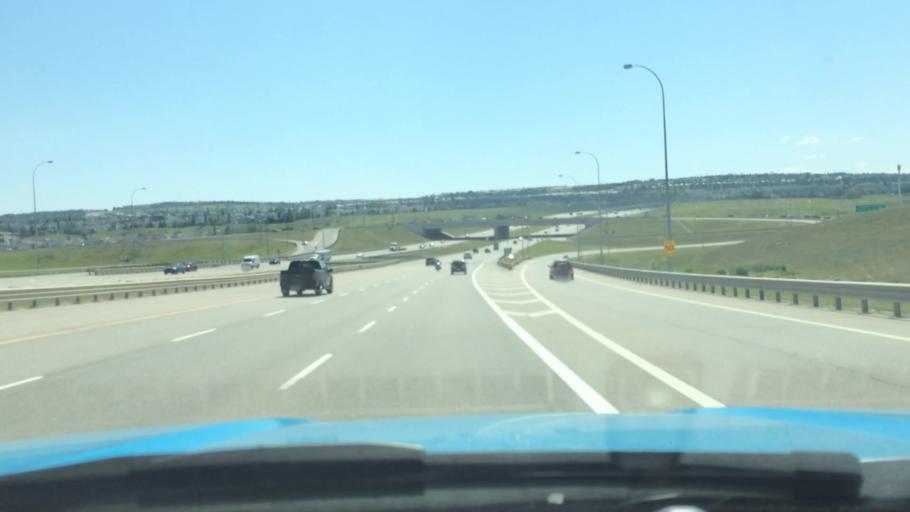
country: CA
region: Alberta
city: Calgary
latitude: 51.1604
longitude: -114.1112
